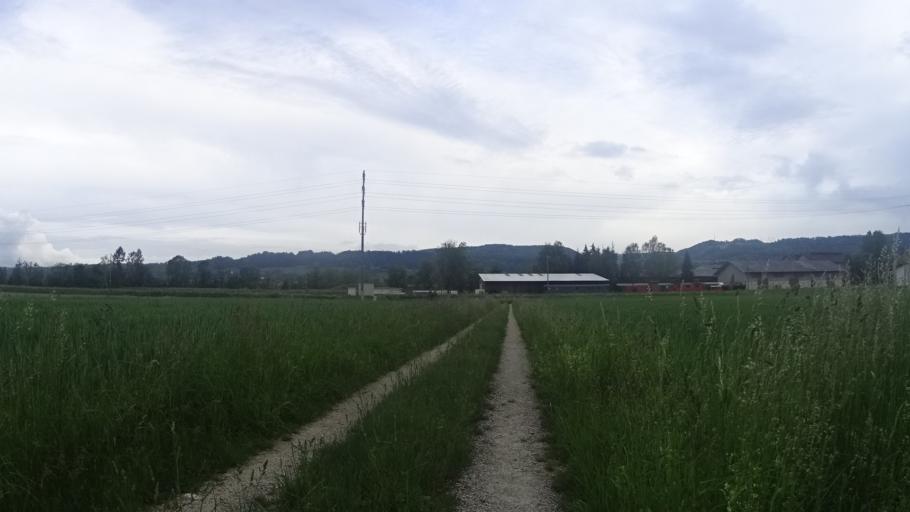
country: CH
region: Aargau
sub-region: Bezirk Zurzach
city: Leibstadt
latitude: 47.6056
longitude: 8.1932
